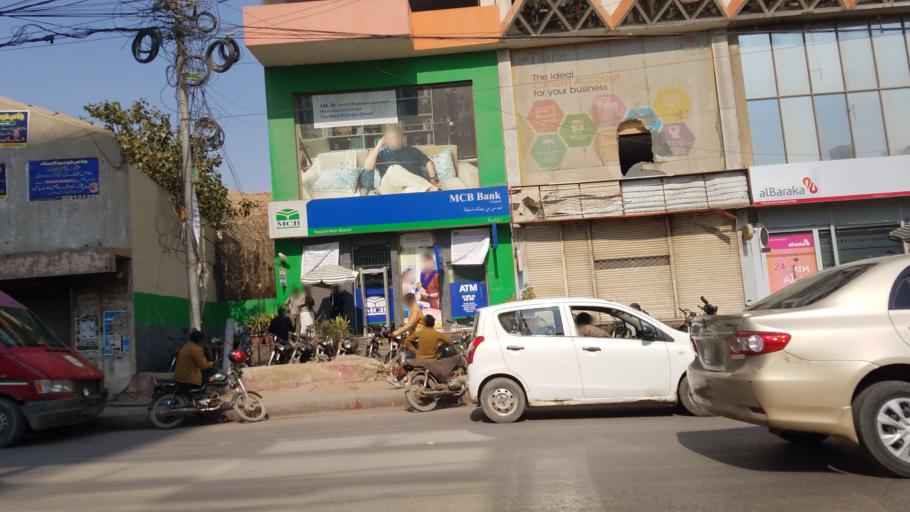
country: PK
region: Sindh
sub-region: Karachi District
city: Karachi
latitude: 24.8489
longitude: 66.9987
